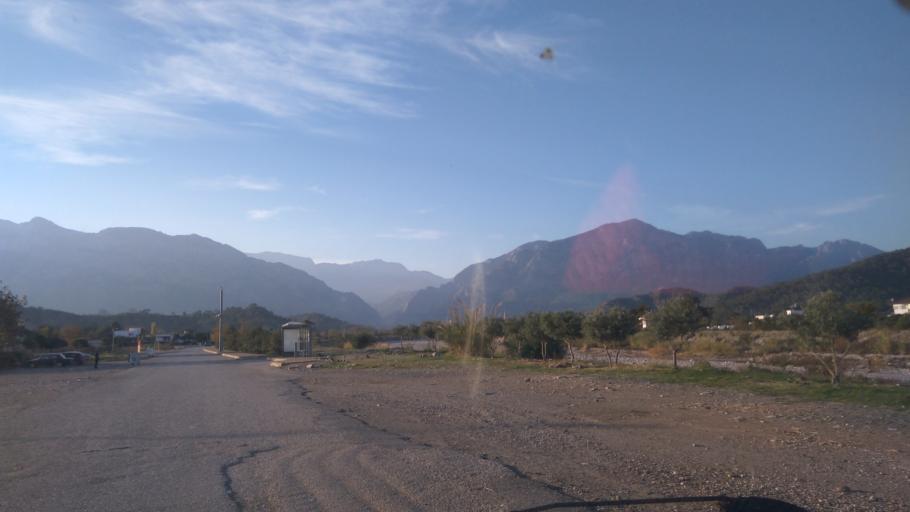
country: TR
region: Antalya
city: Kemer
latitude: 36.5663
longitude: 30.5677
